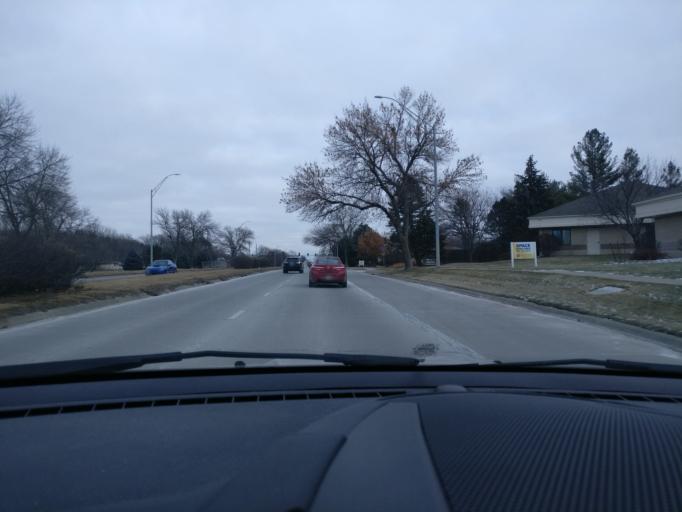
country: US
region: Nebraska
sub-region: Lancaster County
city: Lincoln
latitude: 40.8134
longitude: -96.6187
